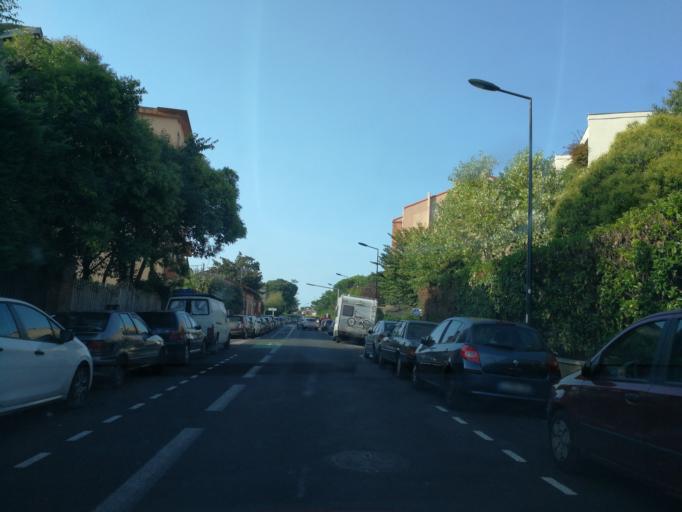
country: FR
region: Midi-Pyrenees
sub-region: Departement de la Haute-Garonne
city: Toulouse
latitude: 43.6227
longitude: 1.4369
